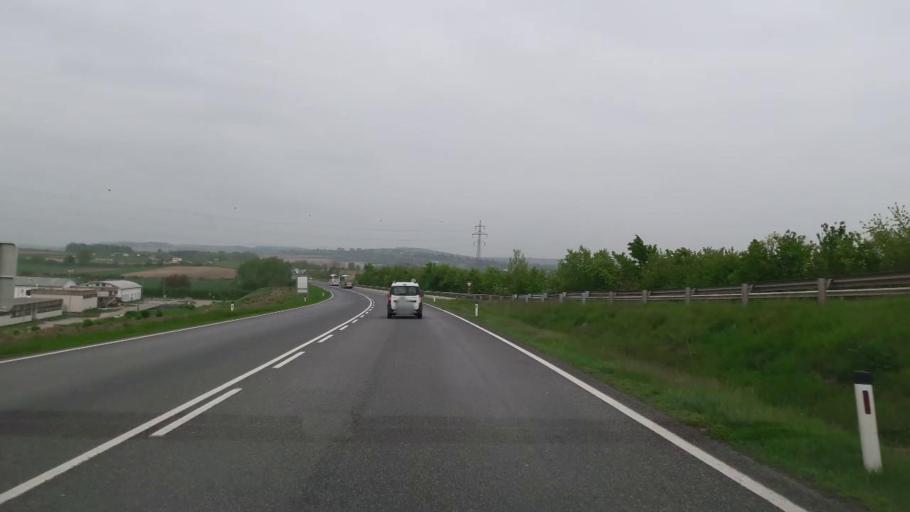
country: AT
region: Lower Austria
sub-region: Politischer Bezirk Hollabrunn
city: Hollabrunn
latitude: 48.5482
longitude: 16.0760
